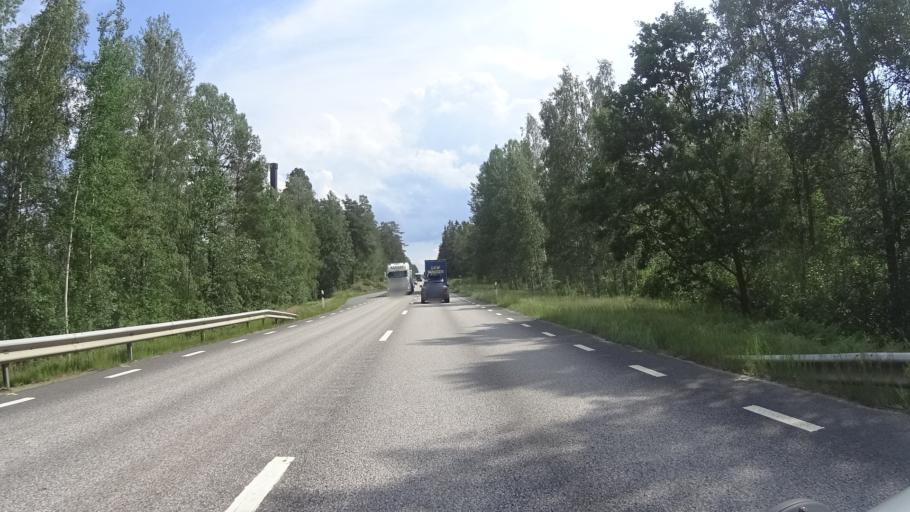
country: SE
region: Kalmar
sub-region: Hultsfreds Kommun
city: Hultsfred
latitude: 57.4827
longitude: 15.8318
